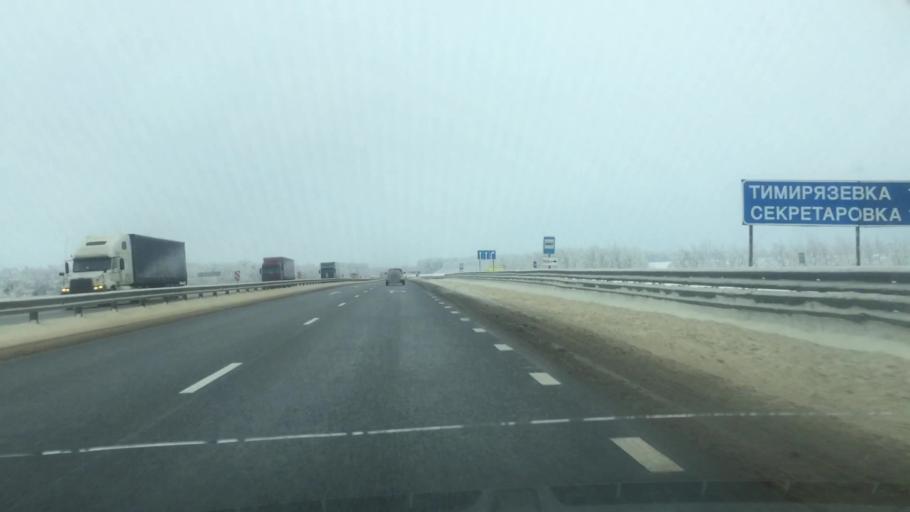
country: RU
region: Lipetsk
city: Zadonsk
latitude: 52.5033
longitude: 38.7554
